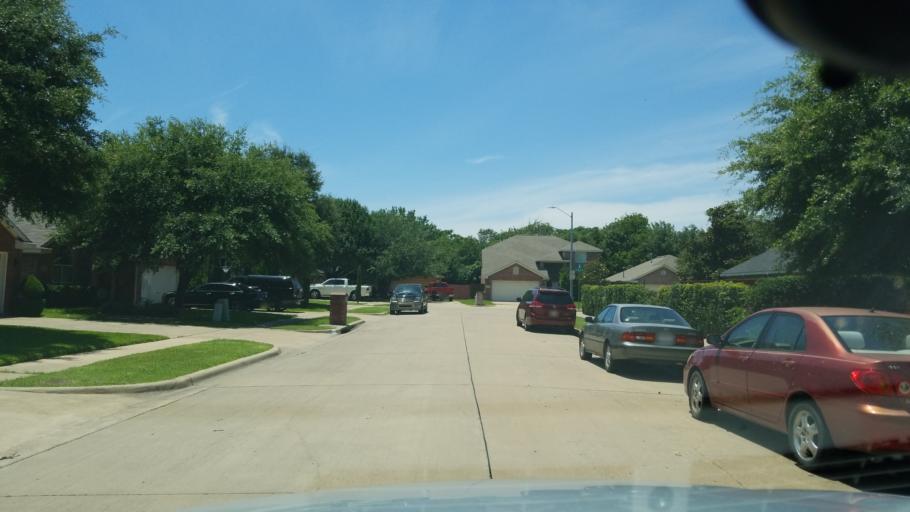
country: US
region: Texas
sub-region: Dallas County
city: Irving
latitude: 32.8211
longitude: -96.9365
